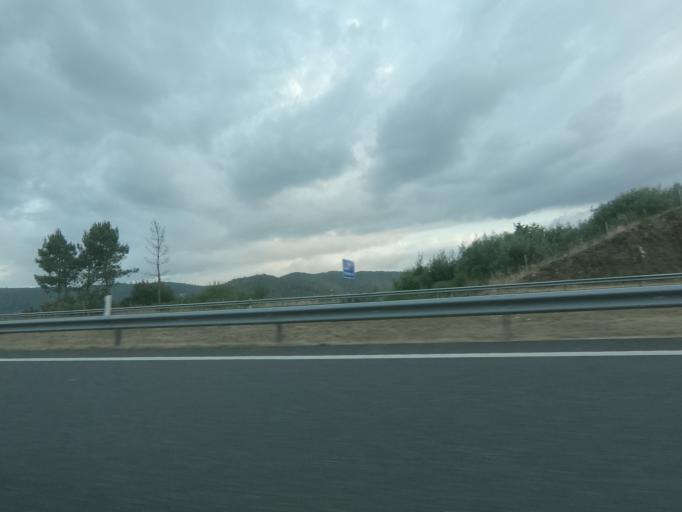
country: ES
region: Galicia
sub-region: Provincia de Ourense
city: Castrelo de Mino
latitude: 42.3327
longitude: -8.0414
